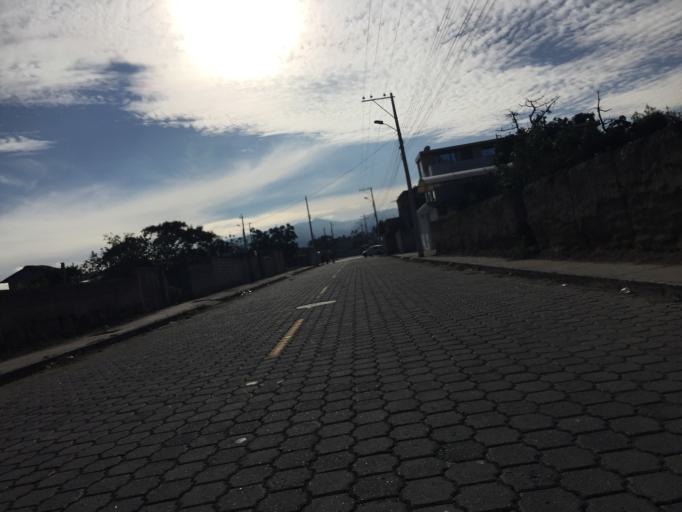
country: EC
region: Imbabura
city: Atuntaqui
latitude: 0.3378
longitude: -78.2008
